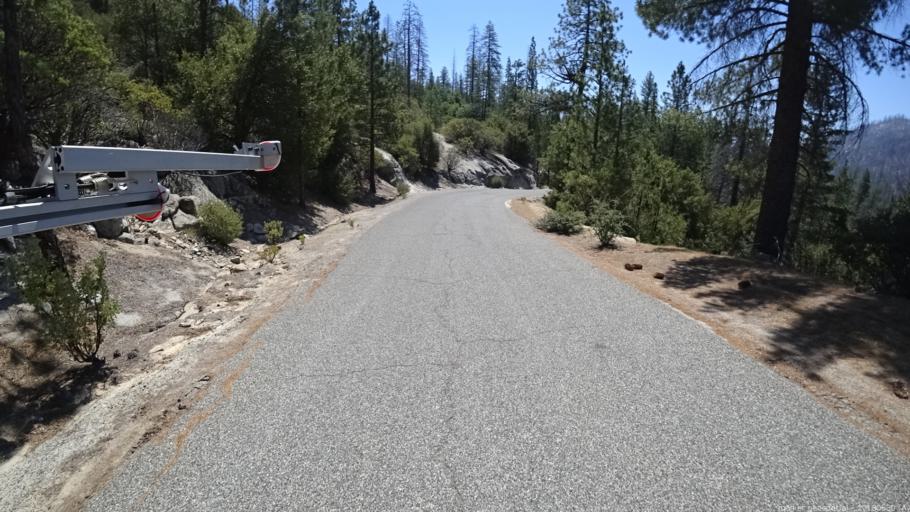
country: US
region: California
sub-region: Madera County
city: Oakhurst
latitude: 37.3699
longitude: -119.3536
